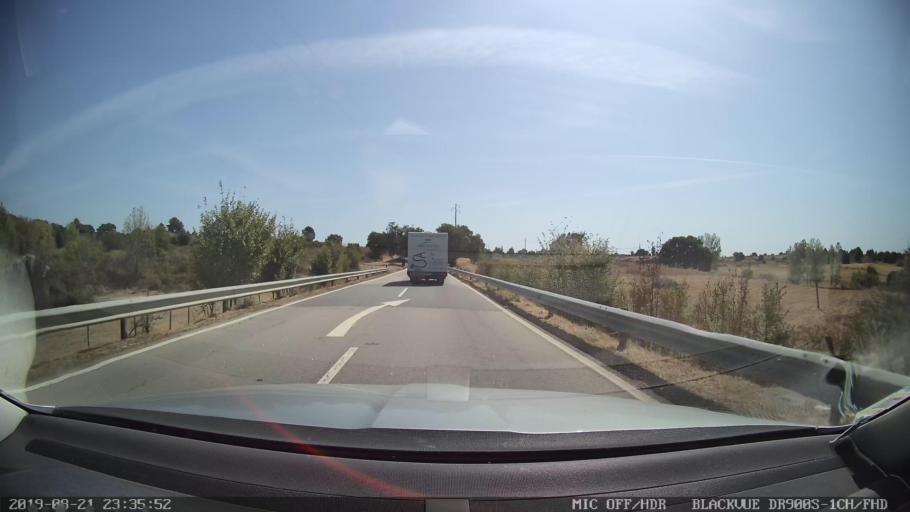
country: PT
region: Guarda
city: Alcains
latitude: 39.8776
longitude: -7.3830
